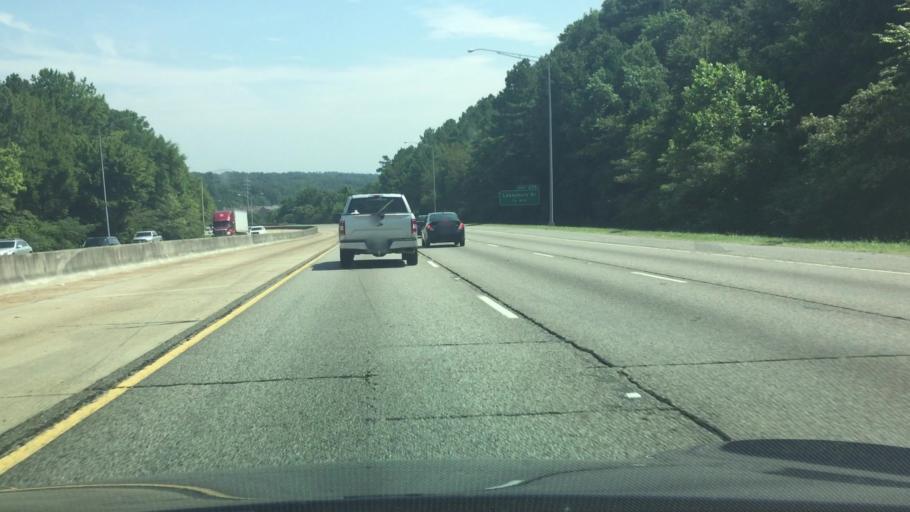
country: US
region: Alabama
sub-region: Jefferson County
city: Vestavia Hills
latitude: 33.4431
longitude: -86.8202
